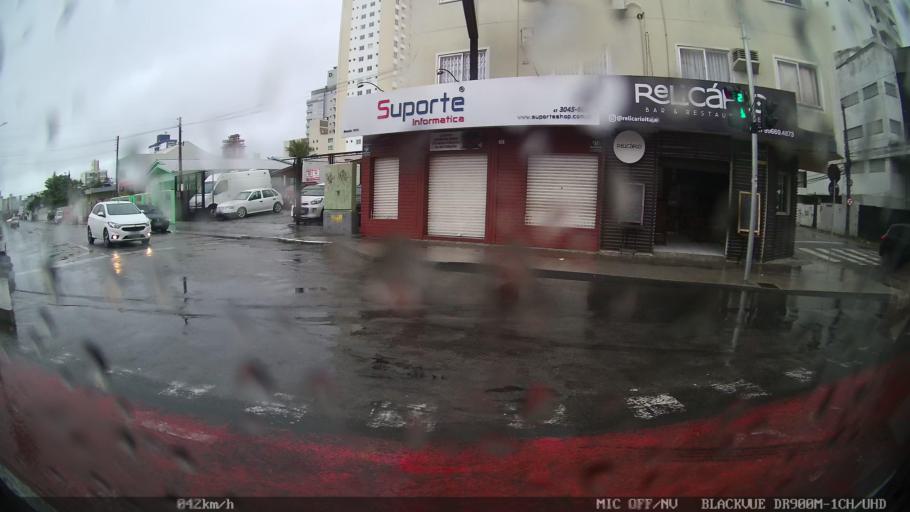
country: BR
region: Santa Catarina
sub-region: Itajai
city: Itajai
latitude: -26.9072
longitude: -48.6739
